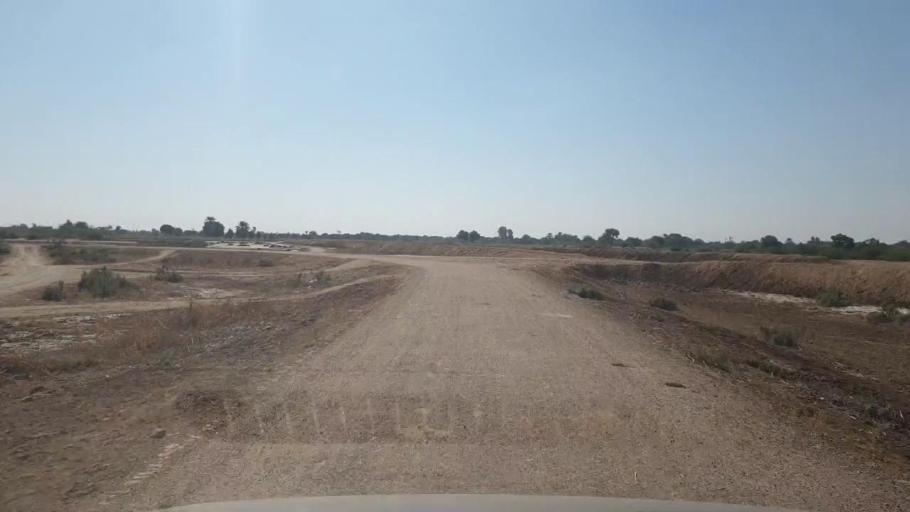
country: PK
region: Sindh
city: Mirwah Gorchani
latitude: 25.2928
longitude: 69.1228
